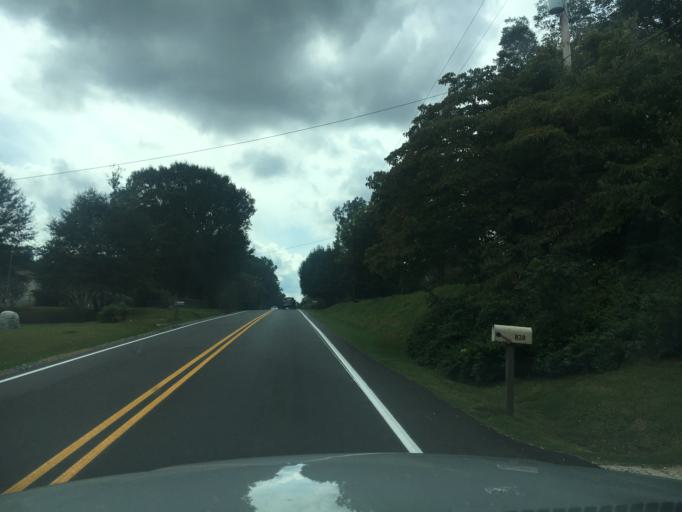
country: US
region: North Carolina
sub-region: Gaston County
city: Bessemer City
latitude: 35.2964
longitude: -81.2317
